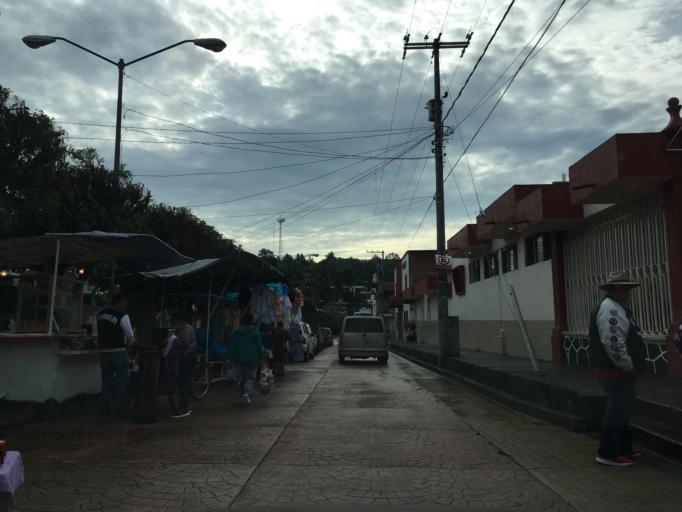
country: MX
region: Michoacan
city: Nuevo San Juan Parangaricutiro
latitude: 19.4171
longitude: -102.1282
